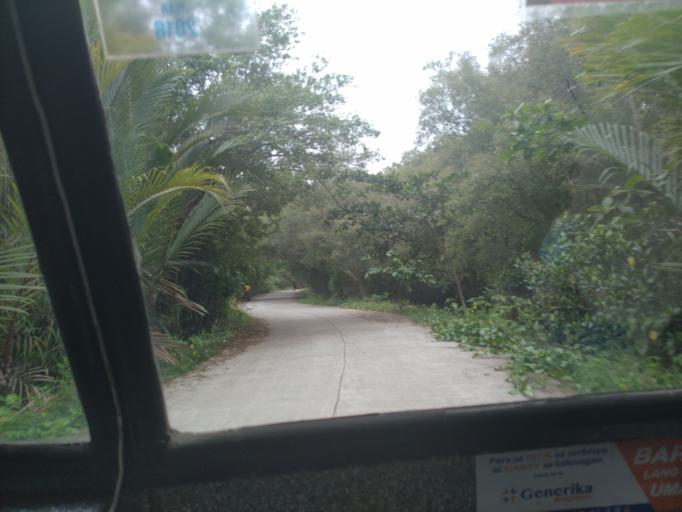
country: PH
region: Central Visayas
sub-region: Province of Negros Oriental
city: Tanjay
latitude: 9.5401
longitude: 123.1557
